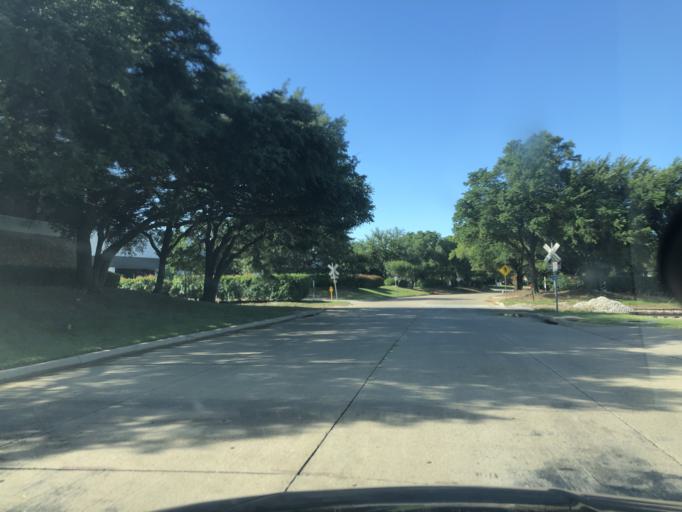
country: US
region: Texas
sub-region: Tarrant County
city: Euless
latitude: 32.8237
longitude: -97.0411
